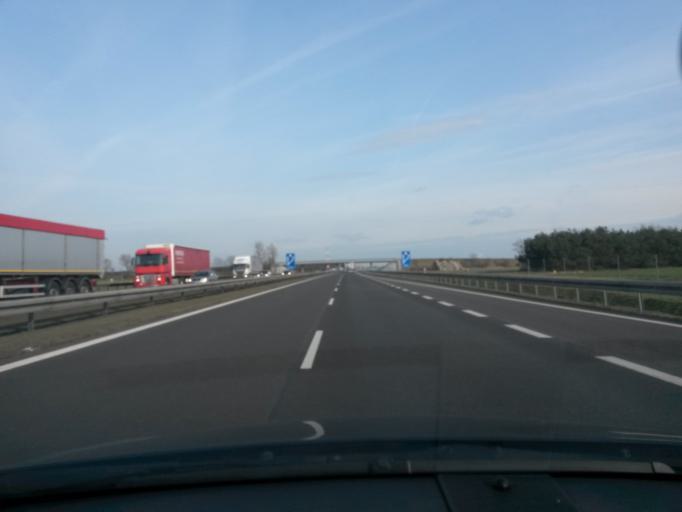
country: PL
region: Greater Poland Voivodeship
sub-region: Powiat slupecki
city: Ladek
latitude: 52.2254
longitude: 17.9365
